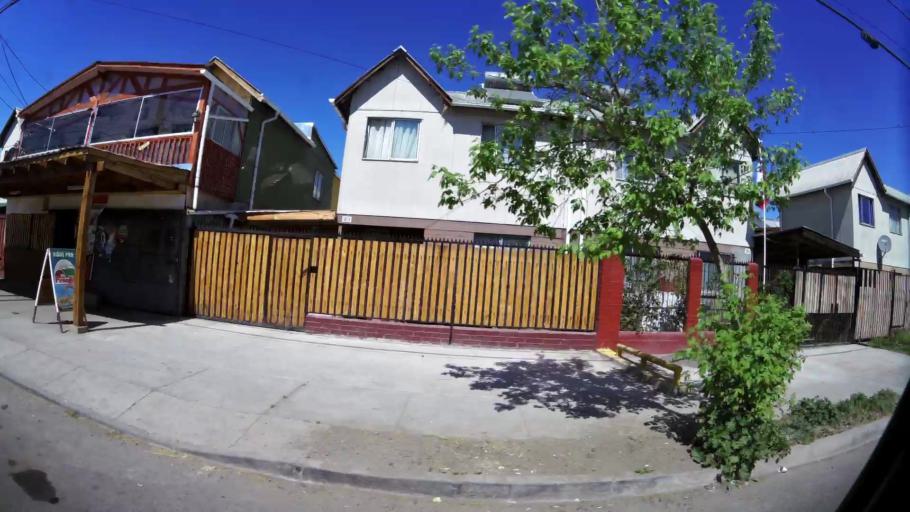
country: CL
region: Santiago Metropolitan
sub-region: Provincia de Talagante
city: Penaflor
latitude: -33.6156
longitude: -70.9040
